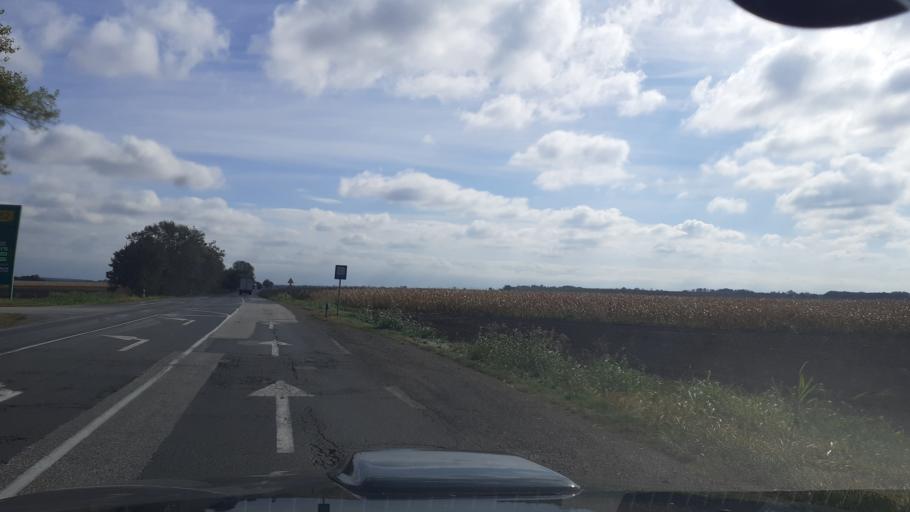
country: HU
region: Bacs-Kiskun
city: Solt
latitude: 46.7975
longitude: 19.0453
